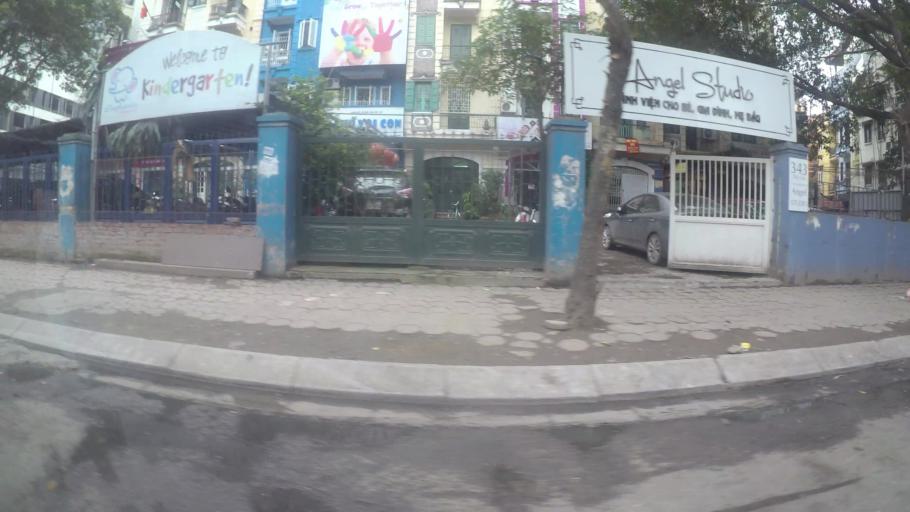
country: VN
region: Ha Noi
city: Cau Giay
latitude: 21.0359
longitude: 105.8174
